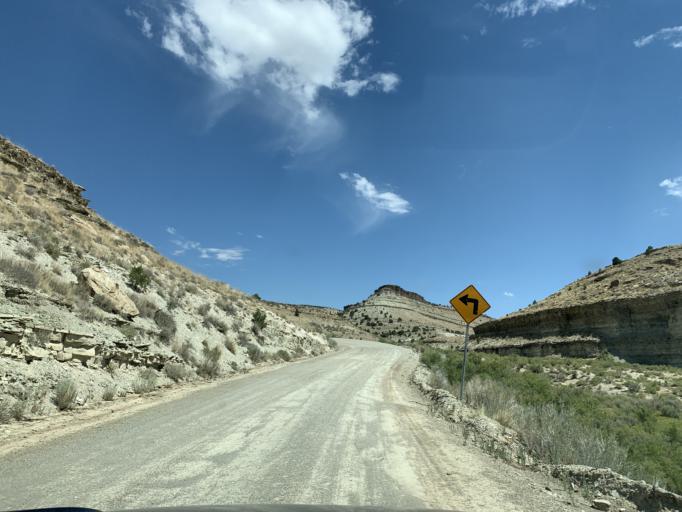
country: US
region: Utah
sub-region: Carbon County
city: East Carbon City
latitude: 39.8454
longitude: -110.2513
